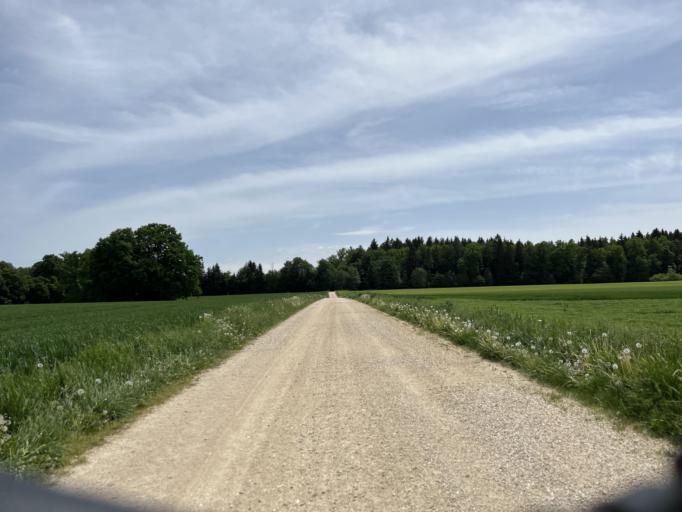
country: DE
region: Baden-Wuerttemberg
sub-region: Tuebingen Region
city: Bingen
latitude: 48.0931
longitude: 9.2647
